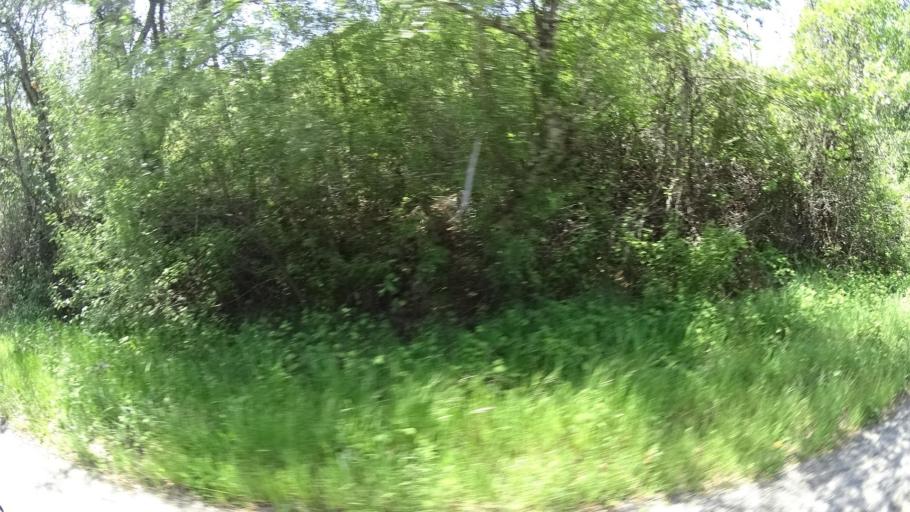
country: US
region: California
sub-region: Humboldt County
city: Redway
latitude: 40.1742
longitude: -123.6061
